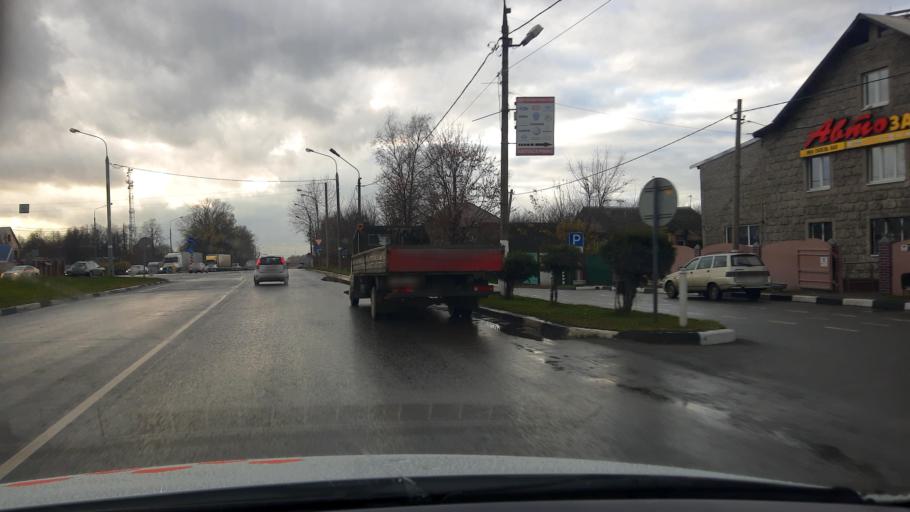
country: RU
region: Moskovskaya
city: Noginsk
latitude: 55.8352
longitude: 38.3849
